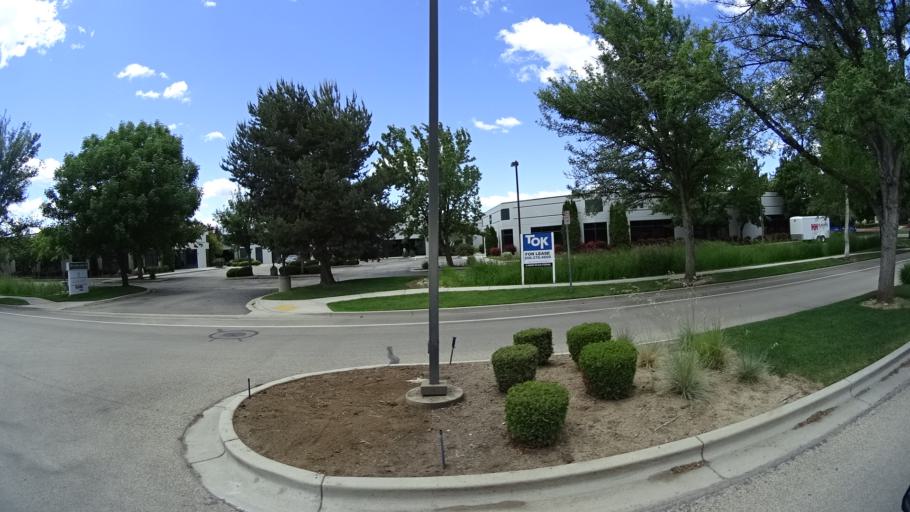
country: US
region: Idaho
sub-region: Ada County
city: Eagle
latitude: 43.6608
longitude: -116.3387
